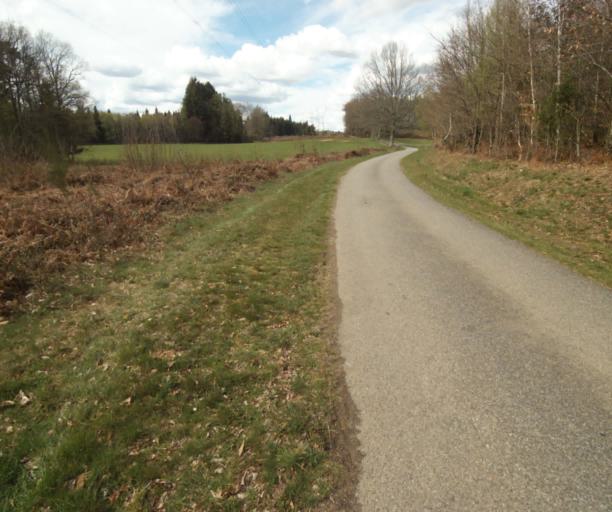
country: FR
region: Limousin
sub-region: Departement de la Correze
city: Argentat
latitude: 45.1877
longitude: 1.9147
